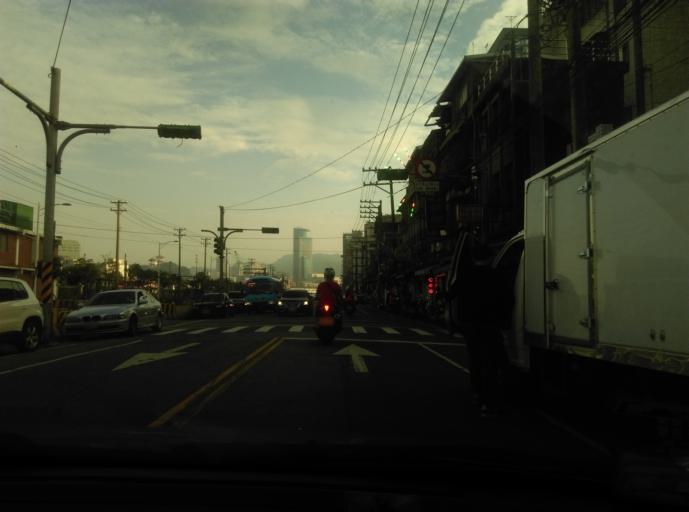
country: TW
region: Taiwan
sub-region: Keelung
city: Keelung
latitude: 25.1405
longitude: 121.7394
